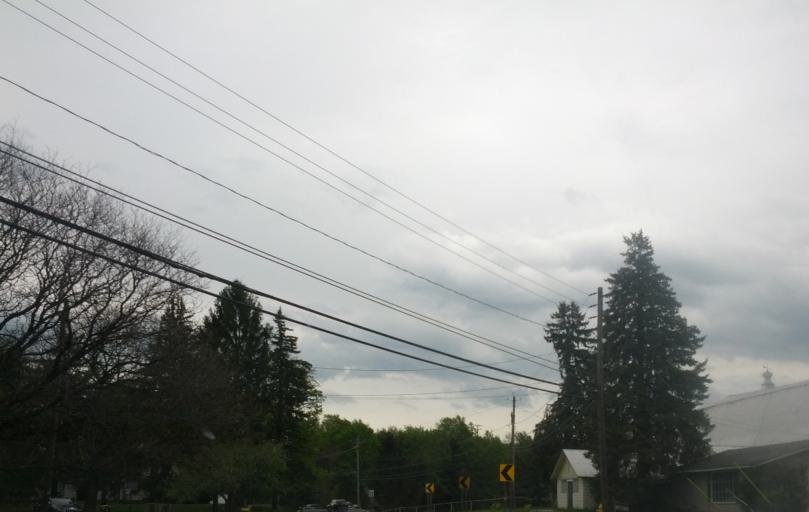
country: US
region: New York
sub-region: Onondaga County
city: Nedrow
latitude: 42.9920
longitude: -76.0920
